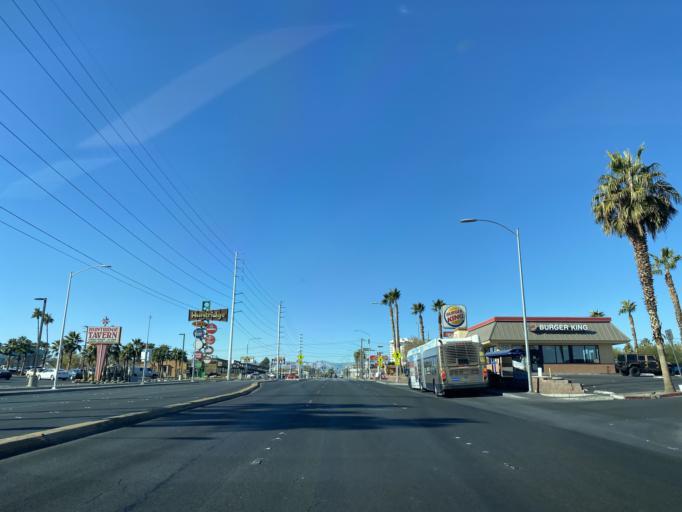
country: US
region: Nevada
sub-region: Clark County
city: Las Vegas
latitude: 36.1589
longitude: -115.1372
